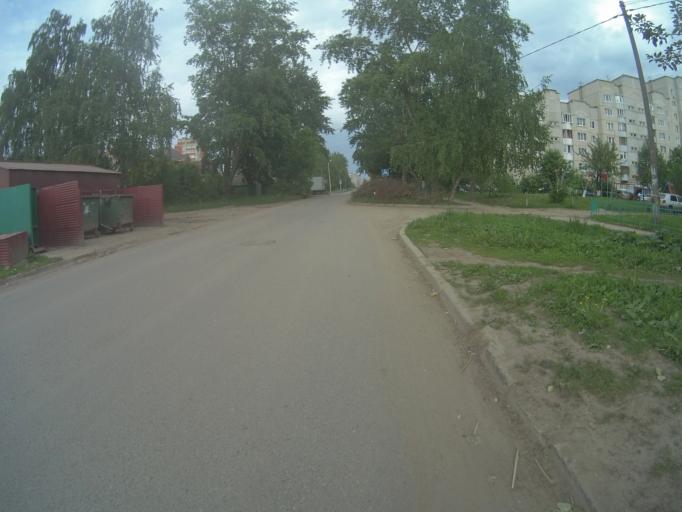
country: RU
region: Vladimir
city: Kommunar
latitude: 56.1635
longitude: 40.4614
